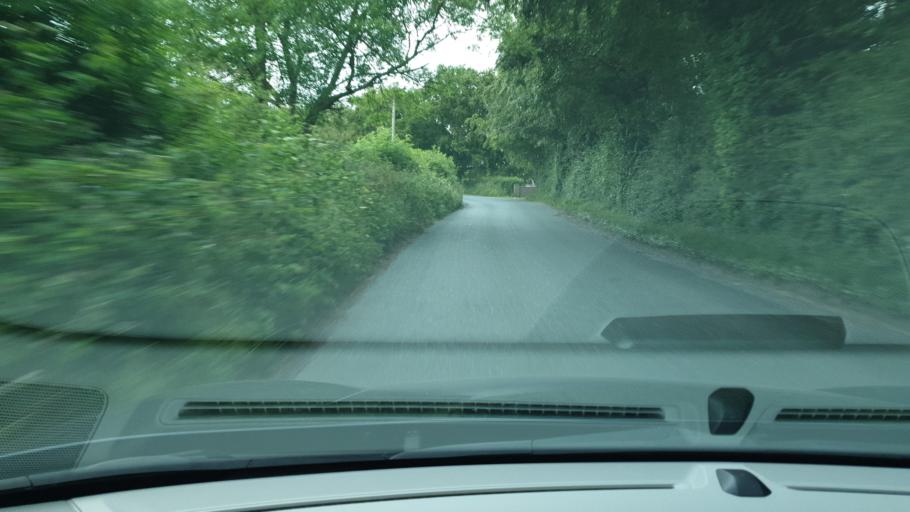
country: IE
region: Leinster
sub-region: An Mhi
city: Ashbourne
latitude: 53.5353
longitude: -6.4311
